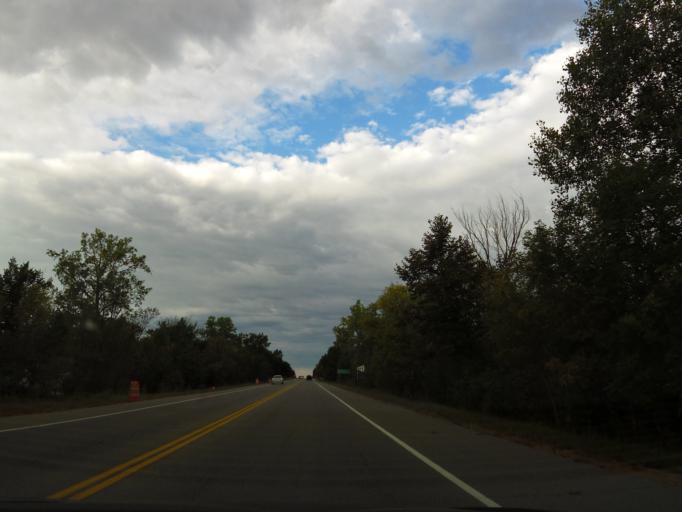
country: US
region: Minnesota
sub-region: Scott County
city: Prior Lake
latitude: 44.7299
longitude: -93.3942
